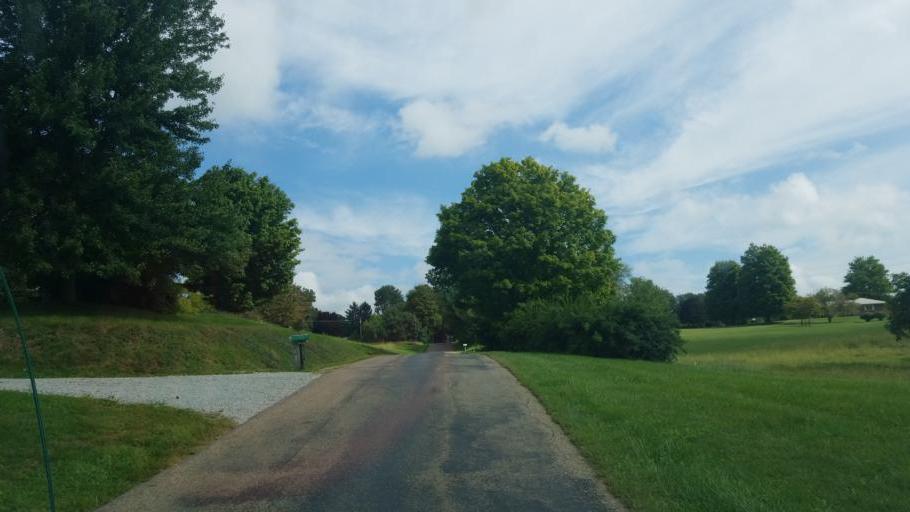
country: US
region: Ohio
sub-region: Knox County
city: Mount Vernon
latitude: 40.4645
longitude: -82.4642
